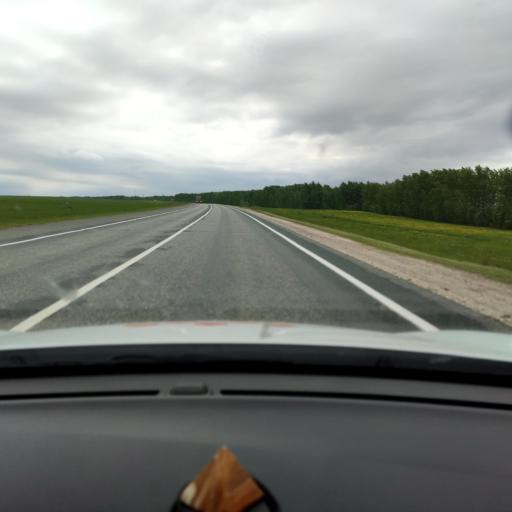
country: RU
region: Tatarstan
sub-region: Alekseyevskiy Rayon
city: Alekseyevskoye
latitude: 55.3926
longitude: 49.8760
